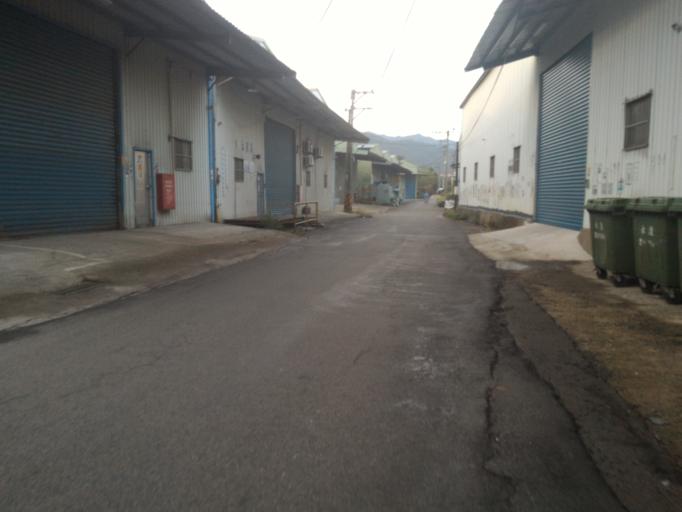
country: TW
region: Taiwan
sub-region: Taoyuan
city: Taoyuan
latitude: 24.9482
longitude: 121.3941
